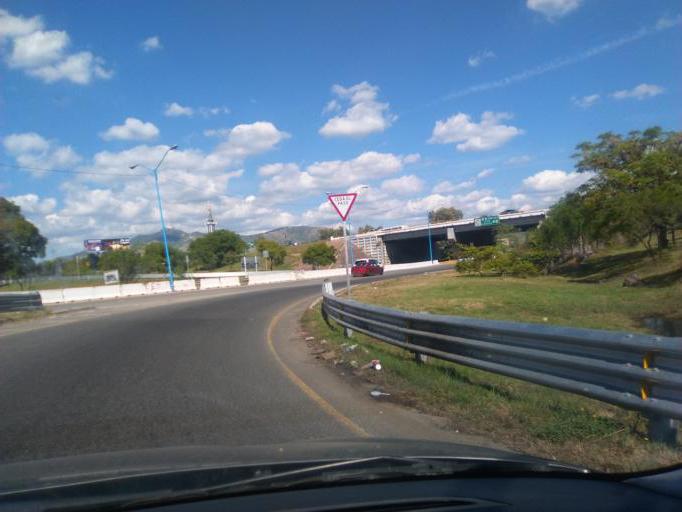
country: MX
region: Guanajuato
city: Silao
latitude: 20.9446
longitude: -101.4148
